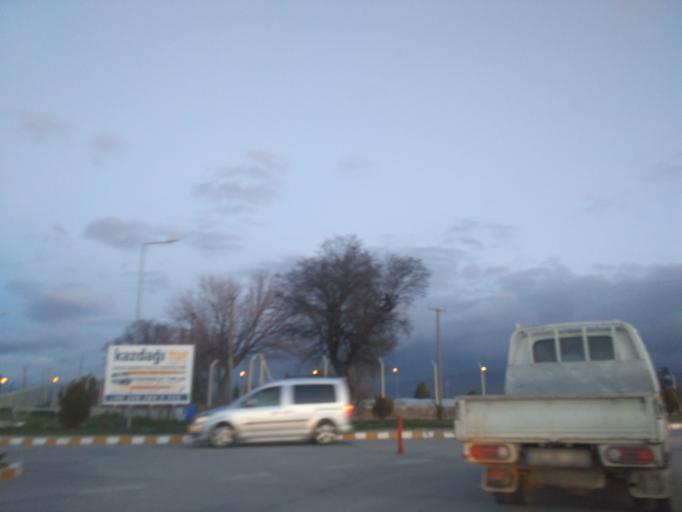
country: TR
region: Balikesir
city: Edremit
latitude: 39.5482
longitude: 27.0134
